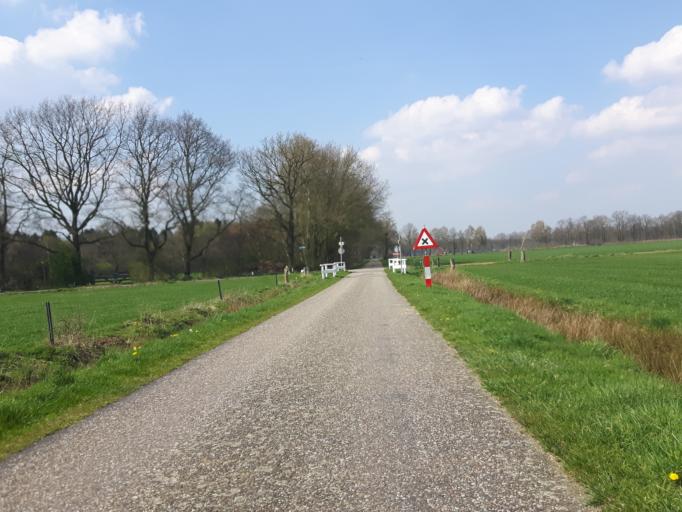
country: NL
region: Overijssel
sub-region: Gemeente Enschede
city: Enschede
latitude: 52.1865
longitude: 6.8278
